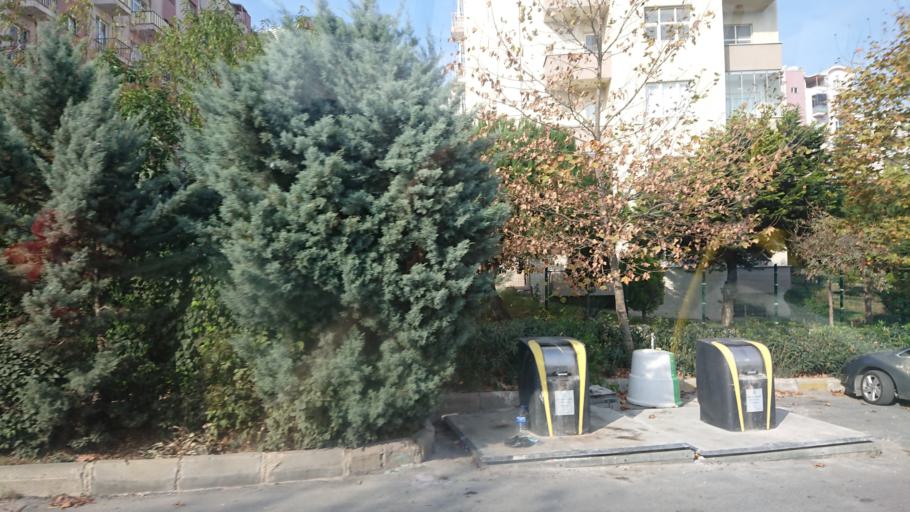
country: TR
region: Istanbul
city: Esenyurt
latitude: 41.0725
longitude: 28.6667
